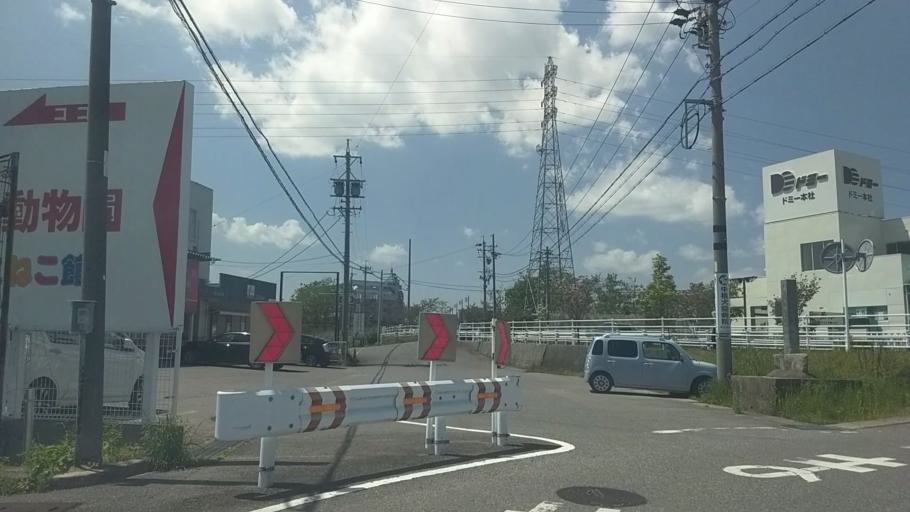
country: JP
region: Aichi
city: Okazaki
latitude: 34.9396
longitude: 137.1881
